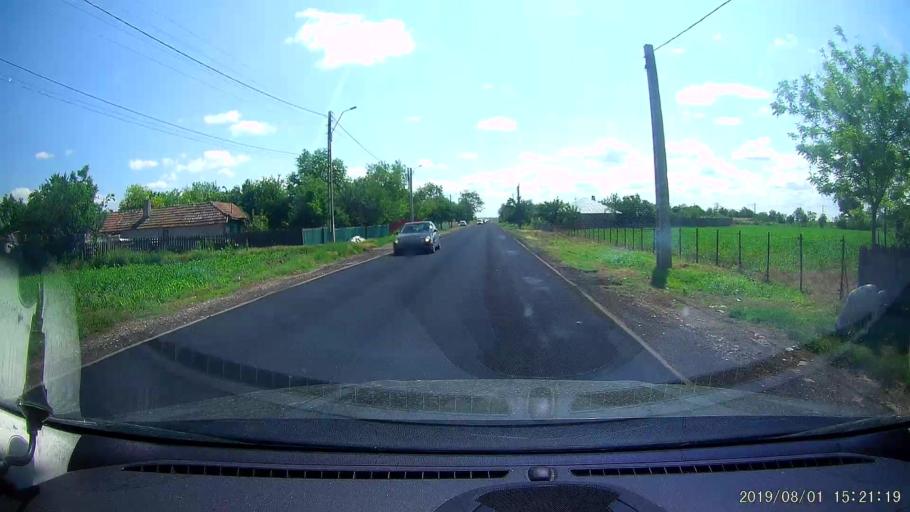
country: RO
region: Braila
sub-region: Comuna Tufesti
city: Tufesti
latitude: 45.0711
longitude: 27.7976
